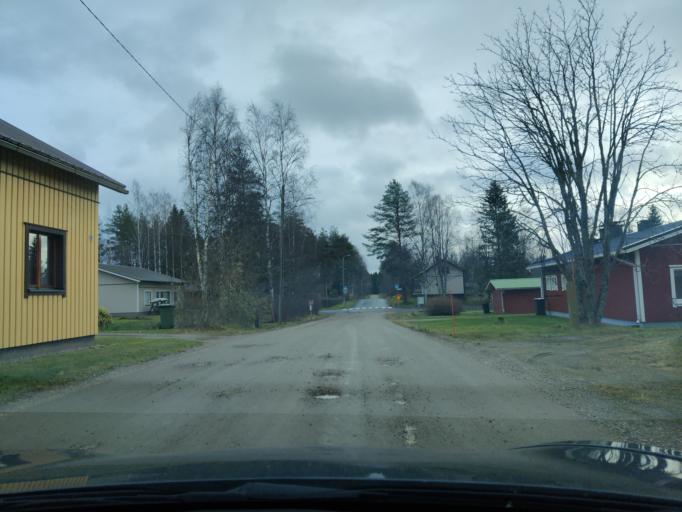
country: FI
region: Northern Savo
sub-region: Ylae-Savo
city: Kiuruvesi
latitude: 63.6479
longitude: 26.6313
